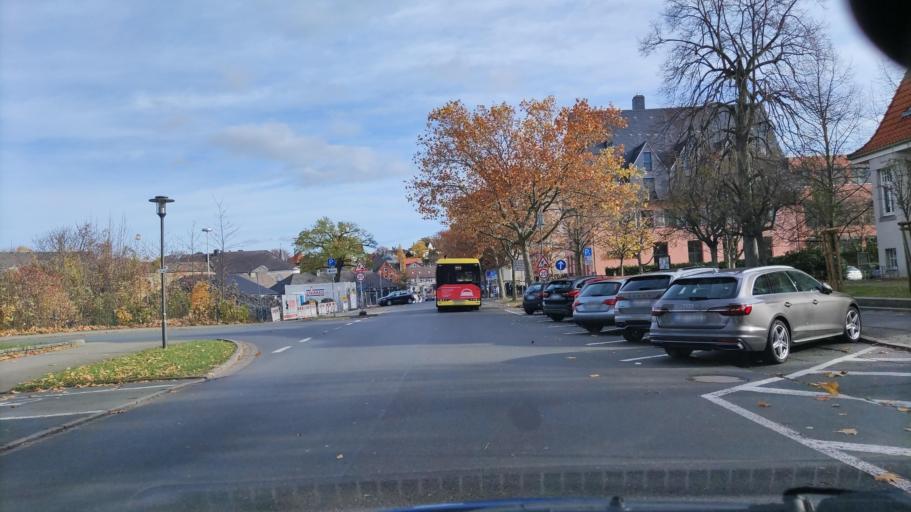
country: DE
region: Lower Saxony
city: Goslar
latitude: 51.9100
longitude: 10.4218
